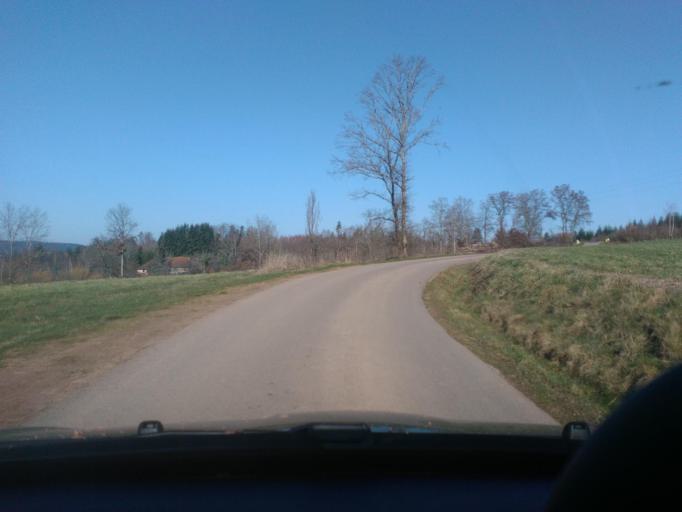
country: FR
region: Lorraine
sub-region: Departement des Vosges
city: Moyenmoutier
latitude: 48.3616
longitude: 6.9185
